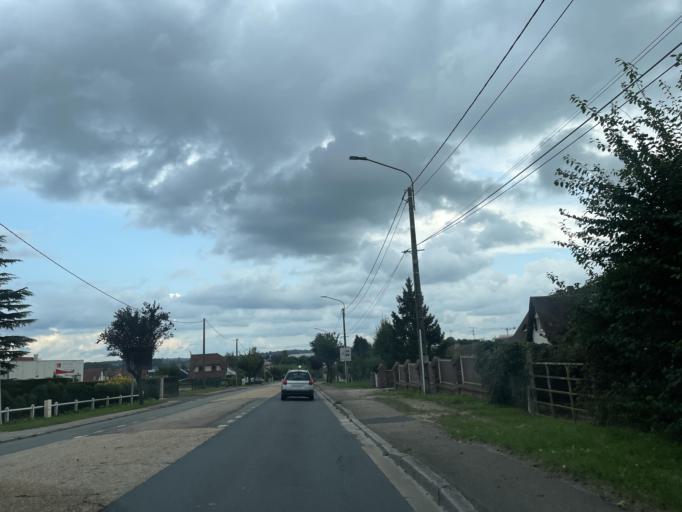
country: FR
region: Haute-Normandie
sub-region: Departement de la Seine-Maritime
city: Gournay-en-Bray
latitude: 49.4849
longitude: 1.7050
